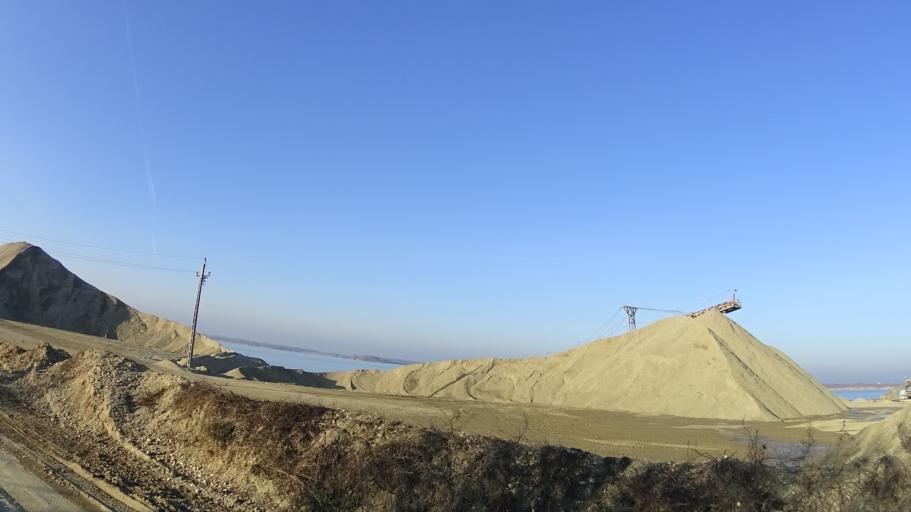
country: HU
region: Borsod-Abauj-Zemplen
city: Onod
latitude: 47.9824
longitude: 20.8851
